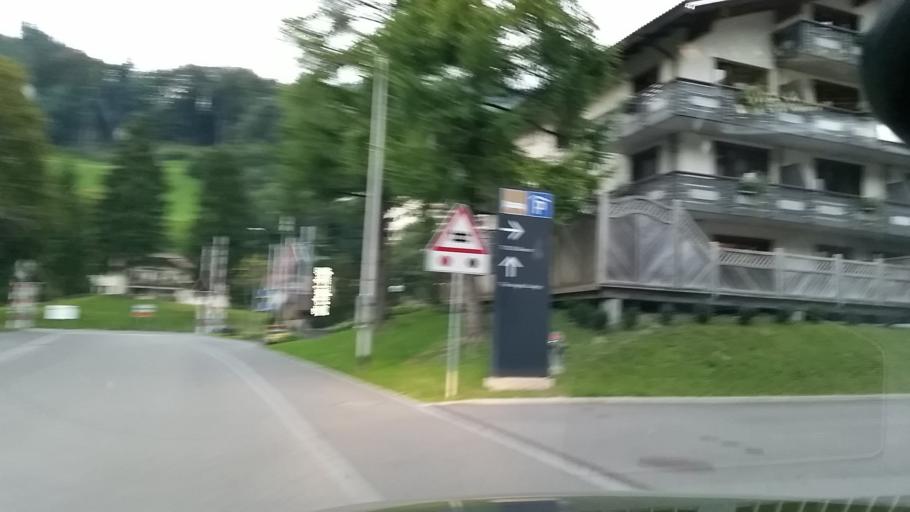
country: CH
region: Obwalden
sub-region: Obwalden
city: Engelberg
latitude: 46.8193
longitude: 8.3950
